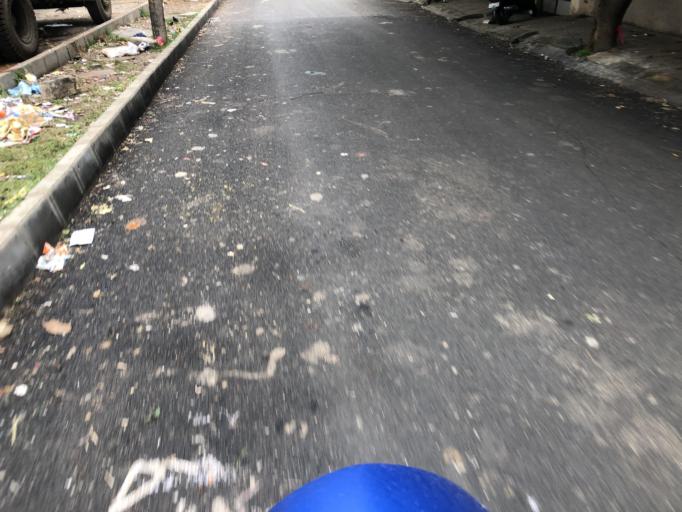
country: IN
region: Karnataka
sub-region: Bangalore Urban
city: Bangalore
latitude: 12.9351
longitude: 77.5460
